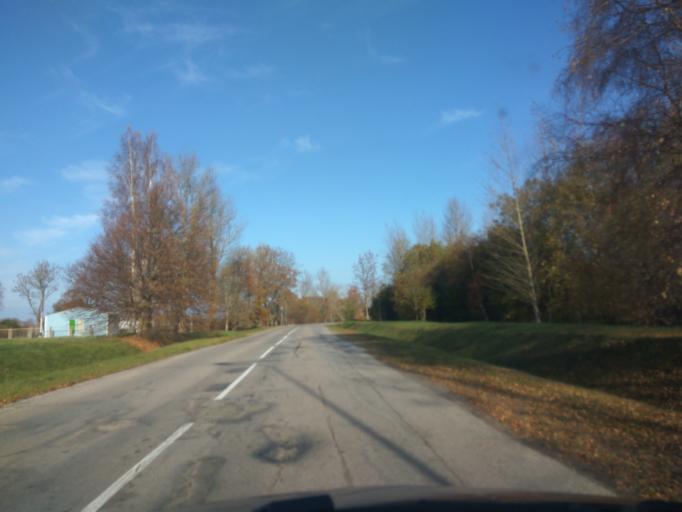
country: LV
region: Ventspils
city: Ventspils
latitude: 57.3682
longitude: 21.5650
